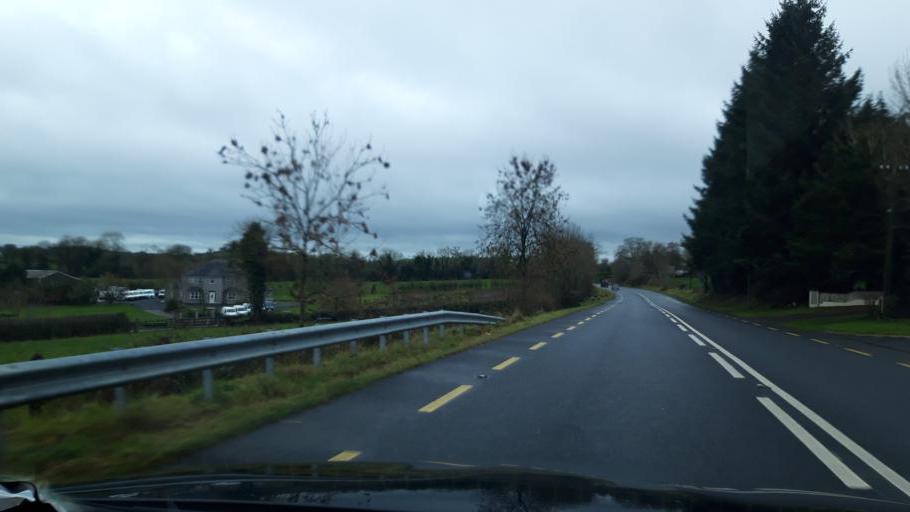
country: IE
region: Ulster
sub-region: County Monaghan
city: Castleblayney
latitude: 54.0853
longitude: -6.6872
